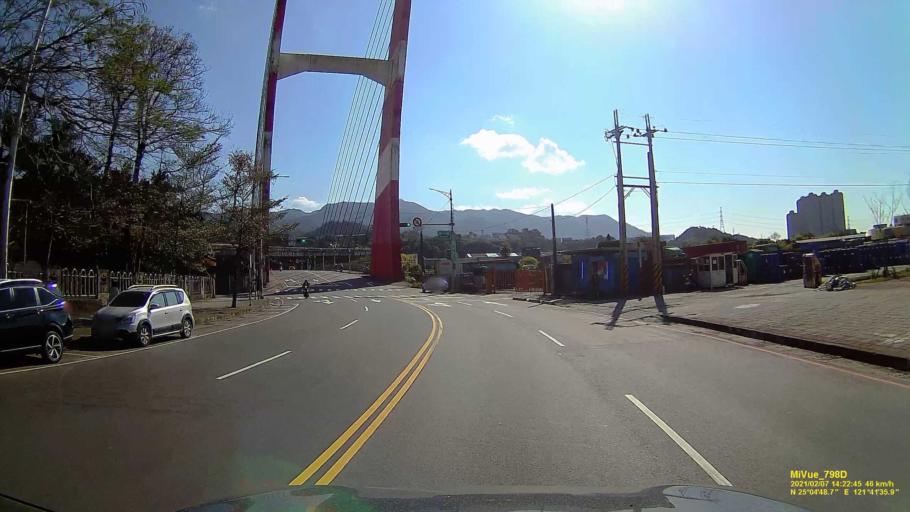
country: TW
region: Taiwan
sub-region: Keelung
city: Keelung
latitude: 25.0799
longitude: 121.6931
